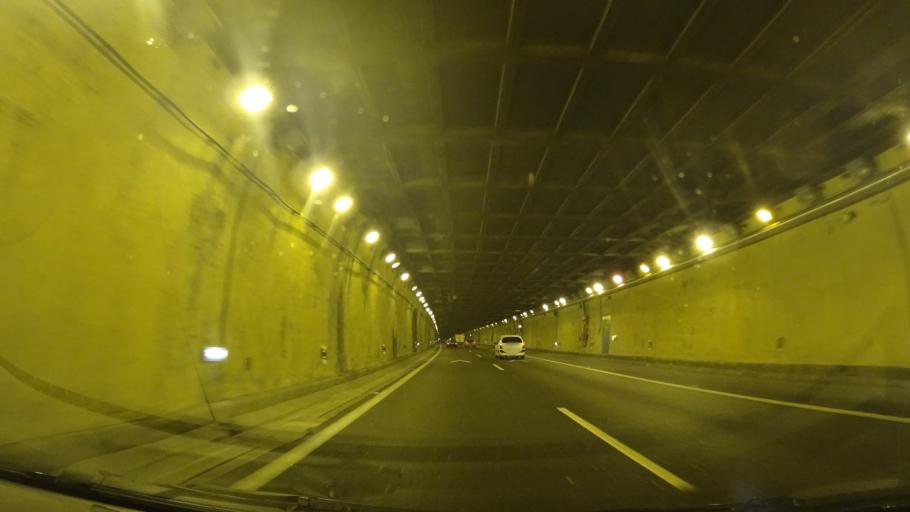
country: ES
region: Madrid
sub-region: Provincia de Madrid
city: Guadarrama
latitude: 40.7016
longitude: -4.1306
